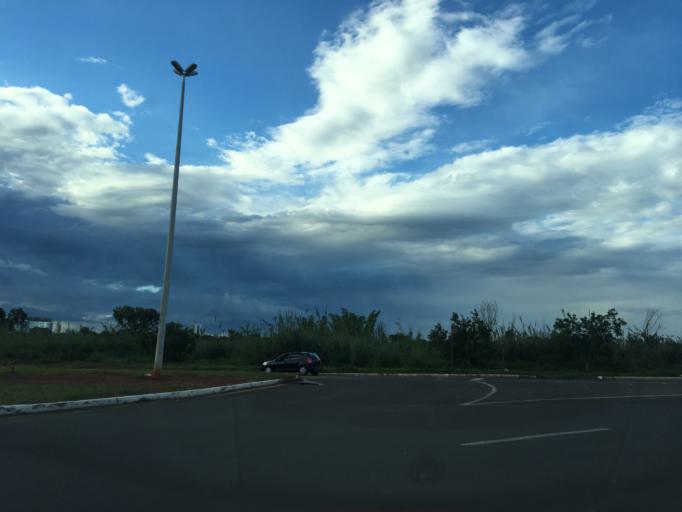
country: BR
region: Federal District
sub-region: Brasilia
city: Brasilia
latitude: -15.8139
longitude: -47.8479
